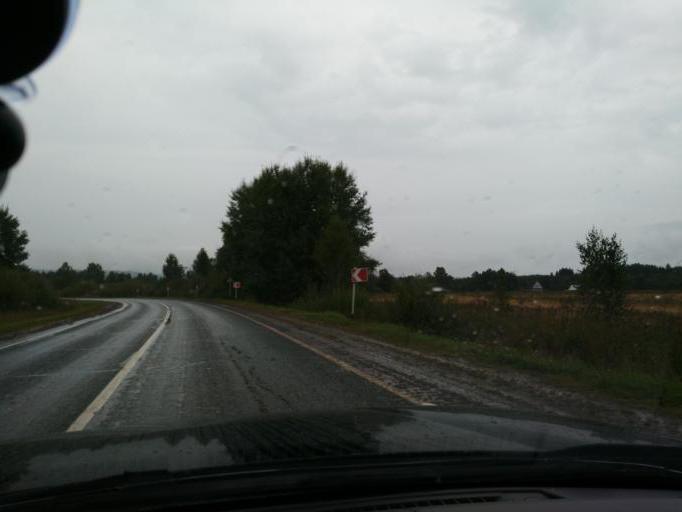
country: RU
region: Perm
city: Yugo-Kamskiy
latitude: 57.5329
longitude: 55.6897
